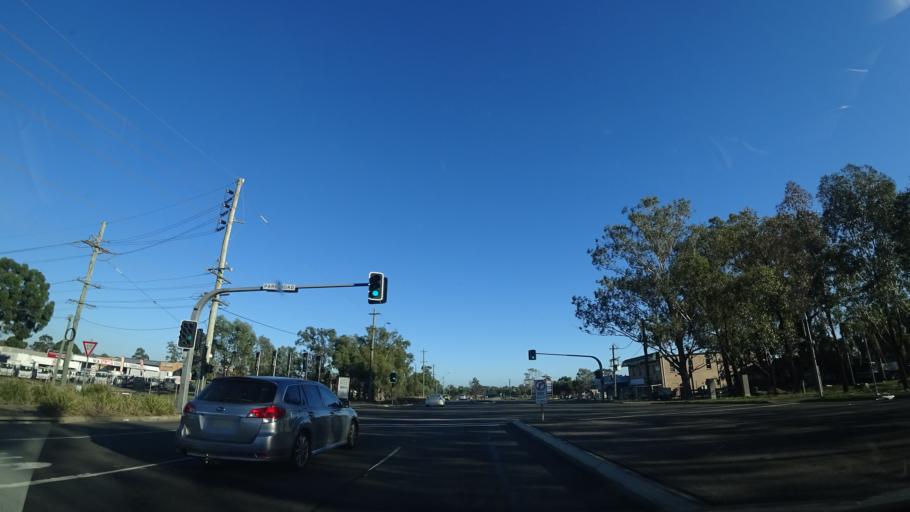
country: AU
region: New South Wales
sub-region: Hawkesbury
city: South Windsor
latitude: -33.6319
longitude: 150.8441
